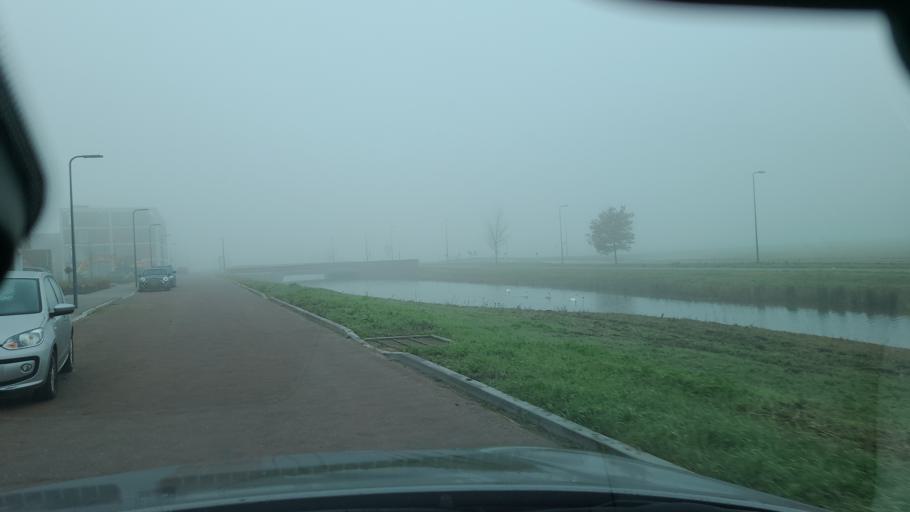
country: NL
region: North Brabant
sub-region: Gemeente 's-Hertogenbosch
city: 's-Hertogenbosch
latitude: 51.7364
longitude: 5.3461
